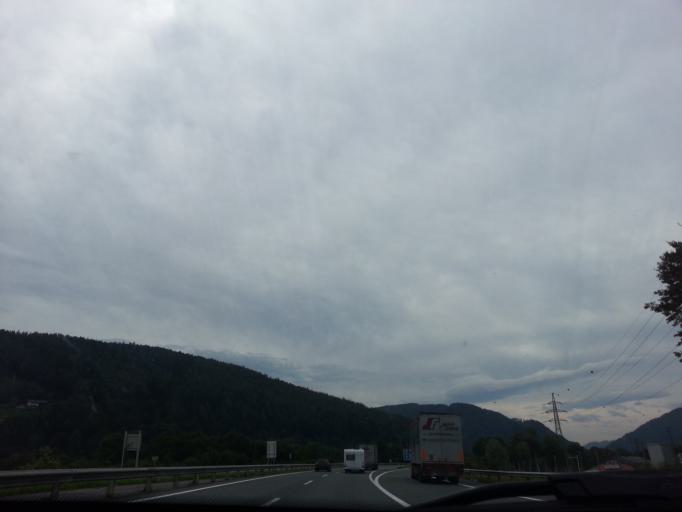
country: AT
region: Styria
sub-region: Politischer Bezirk Graz-Umgebung
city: Deutschfeistritz
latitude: 47.1879
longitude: 15.3305
